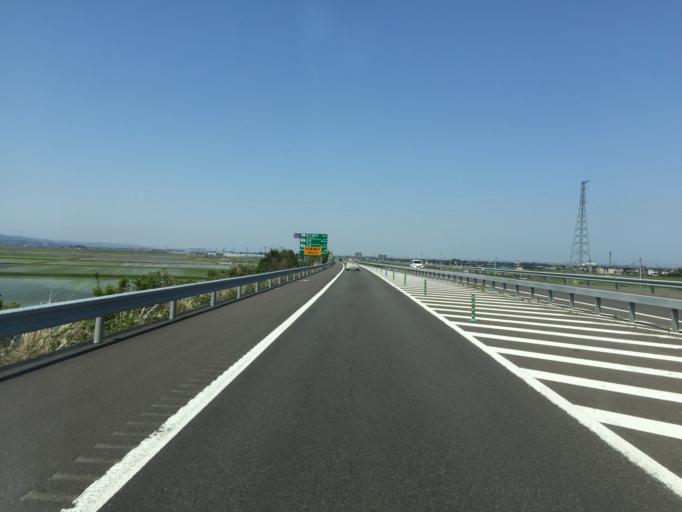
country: JP
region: Miyagi
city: Watari
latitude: 37.9926
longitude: 140.8785
